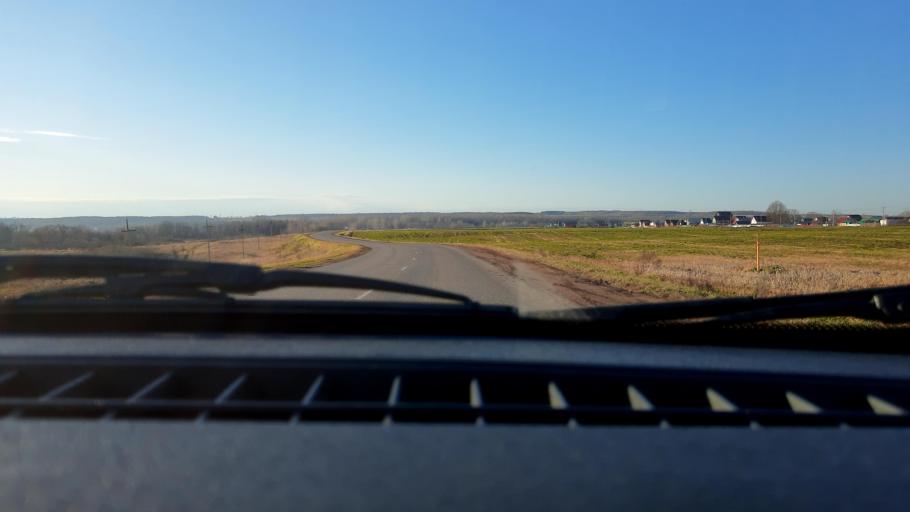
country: RU
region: Bashkortostan
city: Mikhaylovka
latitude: 54.8307
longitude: 55.9588
